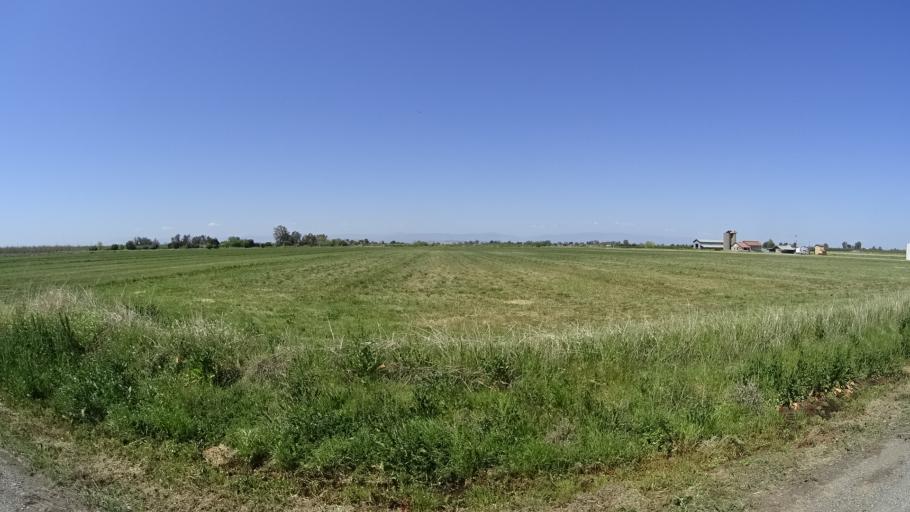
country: US
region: California
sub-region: Glenn County
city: Orland
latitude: 39.7746
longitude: -122.1690
